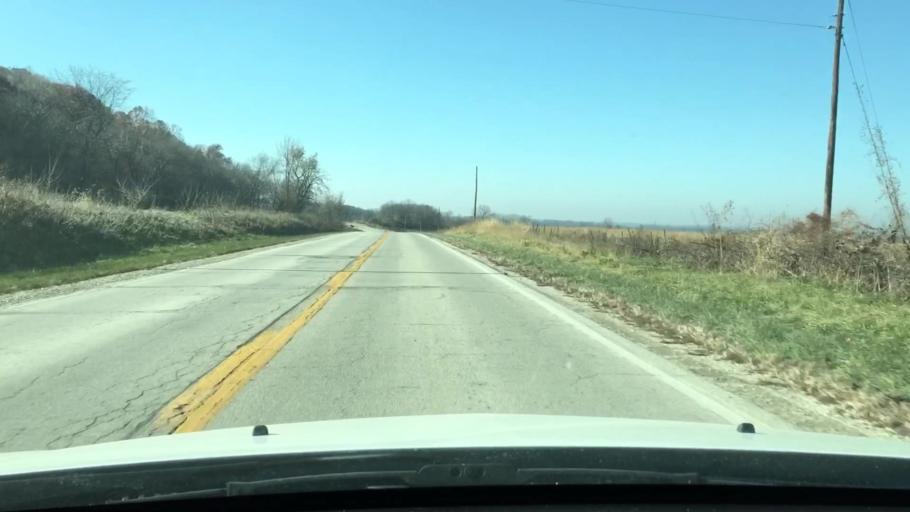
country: US
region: Illinois
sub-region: Morgan County
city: Meredosia
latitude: 39.7416
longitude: -90.5505
